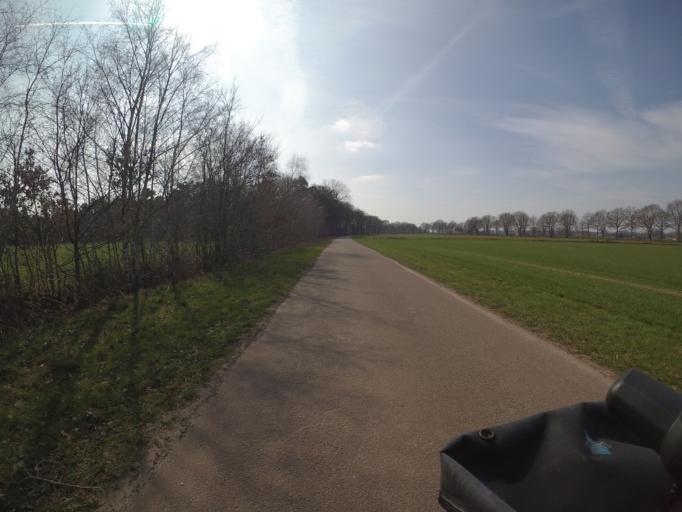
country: NL
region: North Brabant
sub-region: Gemeente Baarle-Nassau
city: Baarle-Nassau
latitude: 51.4990
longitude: 4.9874
